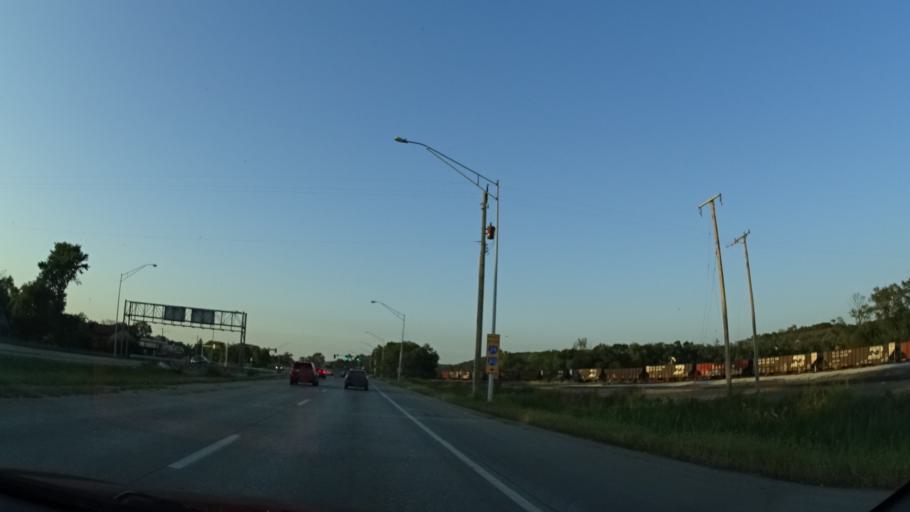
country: US
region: Iowa
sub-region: Pottawattamie County
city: Council Bluffs
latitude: 41.2377
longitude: -95.8512
